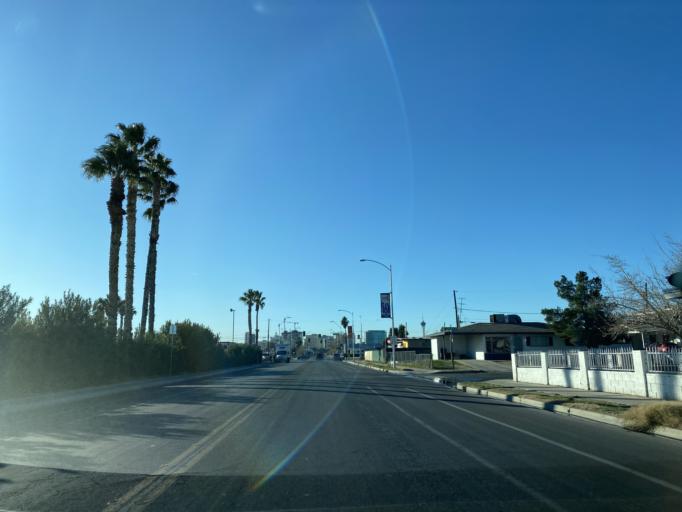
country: US
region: Nevada
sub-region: Clark County
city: Las Vegas
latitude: 36.1898
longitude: -115.1473
